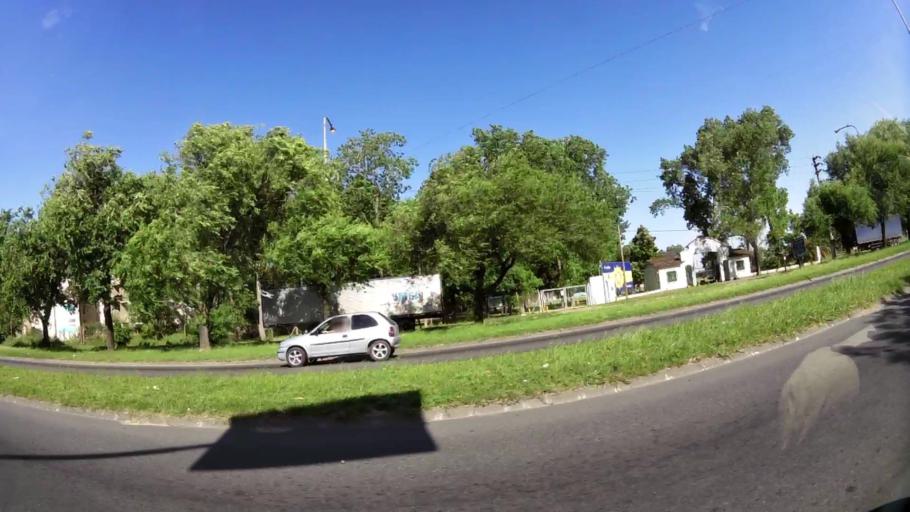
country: AR
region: Buenos Aires
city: Caseros
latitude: -34.5680
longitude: -58.5903
